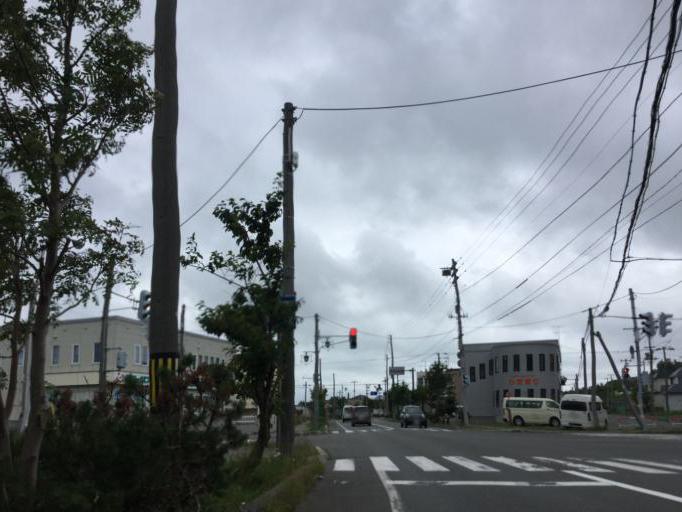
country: JP
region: Hokkaido
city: Wakkanai
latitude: 45.3942
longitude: 141.6991
